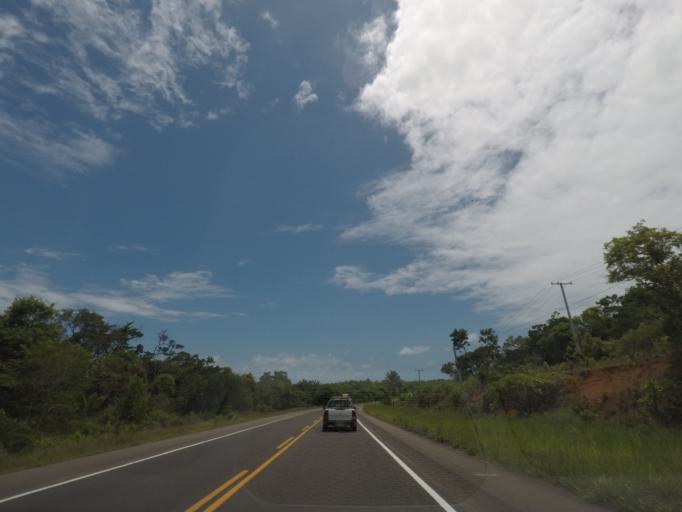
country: BR
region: Bahia
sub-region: Itaparica
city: Itaparica
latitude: -12.9778
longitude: -38.6335
